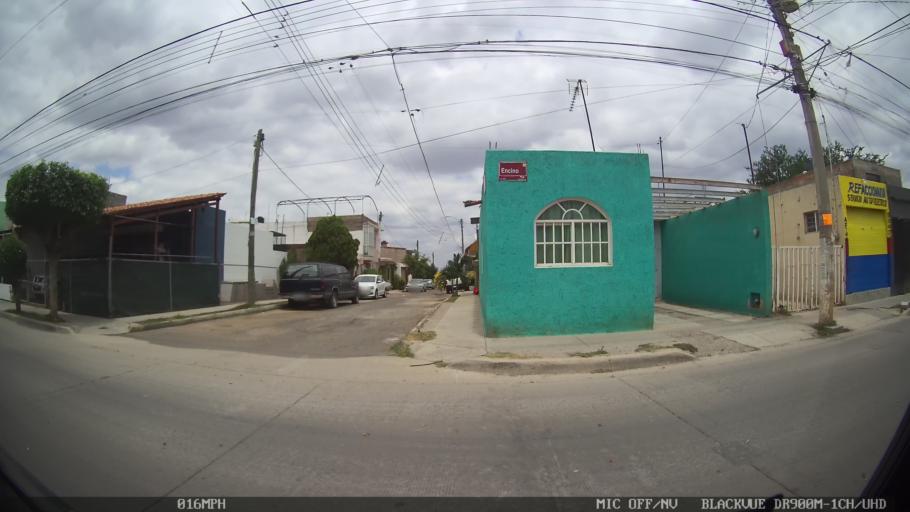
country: MX
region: Jalisco
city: Tonala
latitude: 20.6434
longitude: -103.2539
